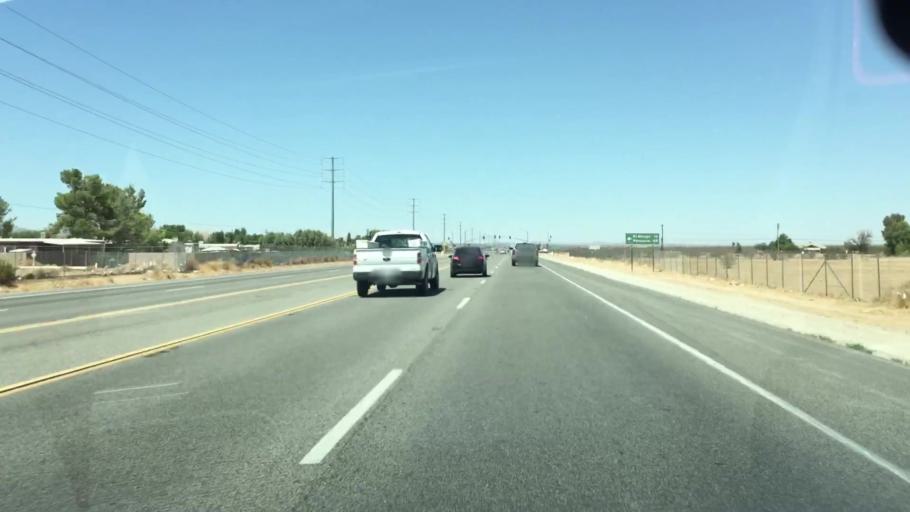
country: US
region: California
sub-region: San Bernardino County
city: Adelanto
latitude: 34.5831
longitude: -117.4133
